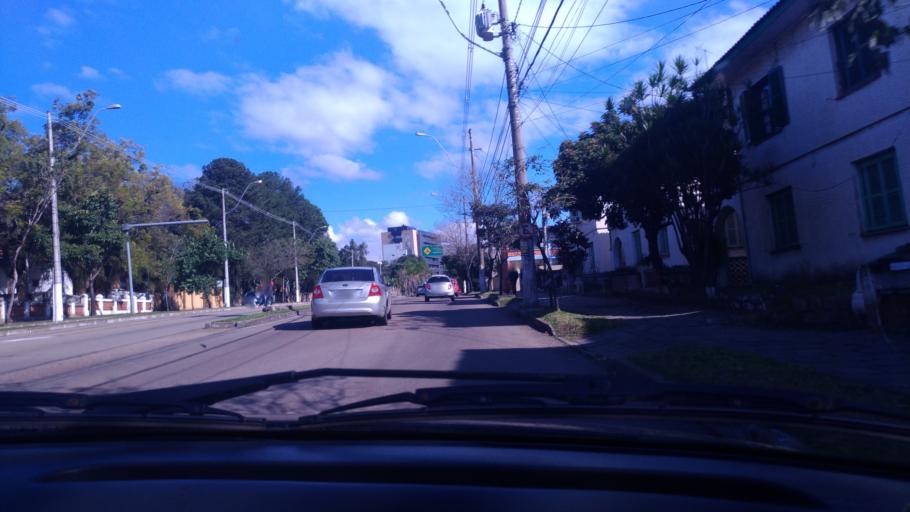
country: BR
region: Rio Grande do Sul
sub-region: Porto Alegre
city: Porto Alegre
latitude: -30.0690
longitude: -51.1883
